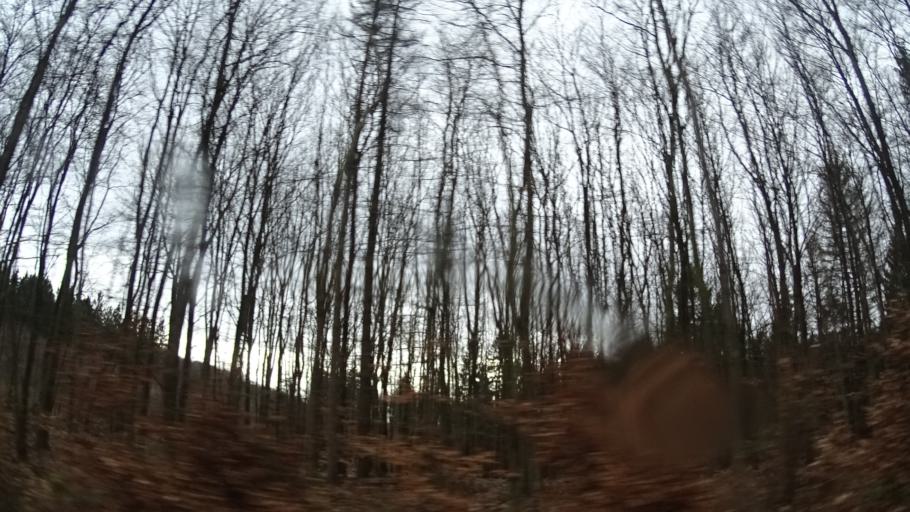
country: DE
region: Rheinland-Pfalz
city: Oberheimbach
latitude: 49.9873
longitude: 7.7776
